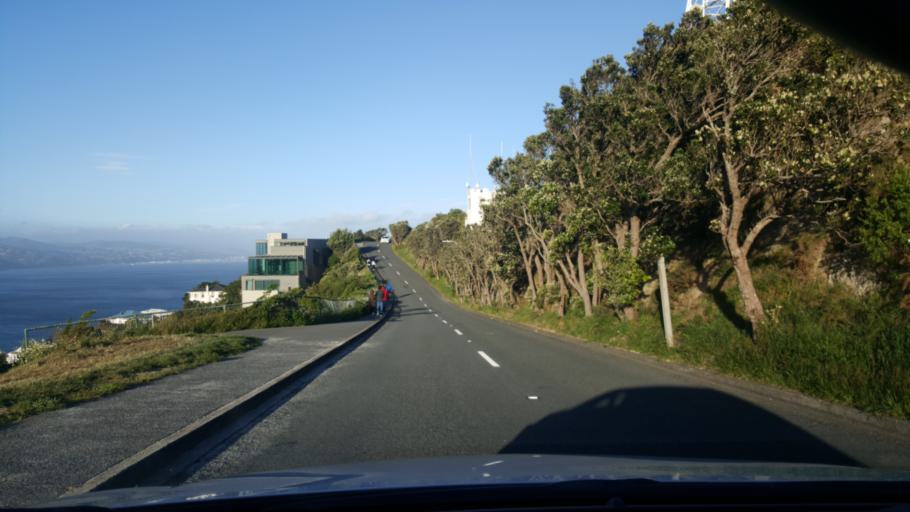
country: NZ
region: Wellington
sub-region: Wellington City
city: Wellington
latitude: -41.2961
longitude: 174.7958
